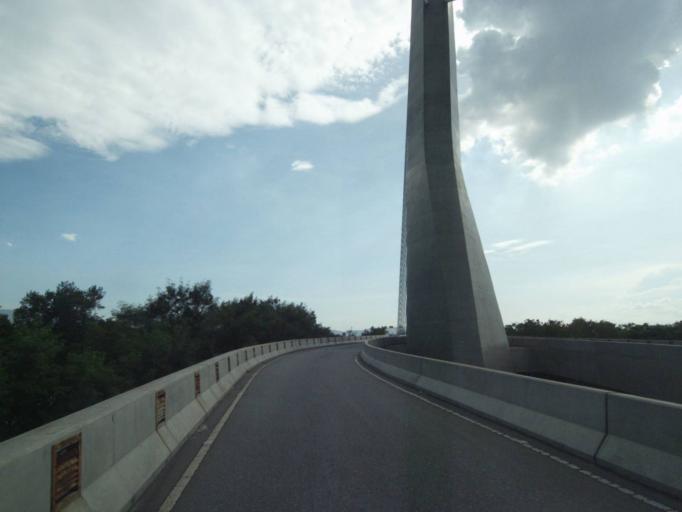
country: BR
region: Rio de Janeiro
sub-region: Rio De Janeiro
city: Rio de Janeiro
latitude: -22.8659
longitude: -43.2309
